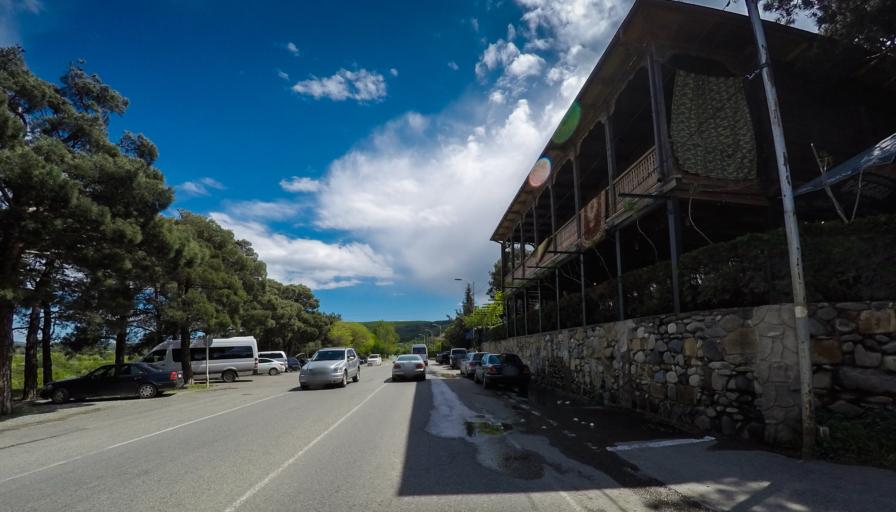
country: GE
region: Mtskheta-Mtianeti
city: Mtskheta
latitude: 41.8292
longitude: 44.7249
